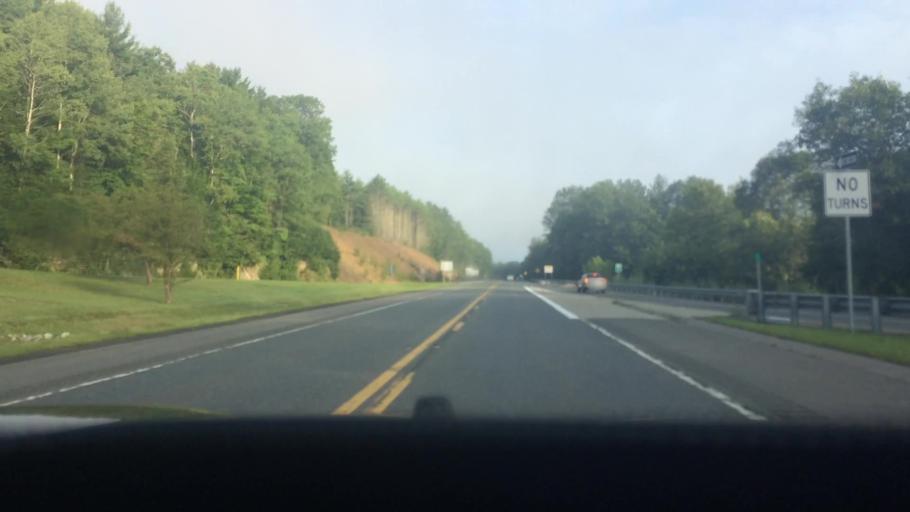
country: US
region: Massachusetts
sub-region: Franklin County
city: Orange
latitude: 42.5926
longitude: -72.3367
